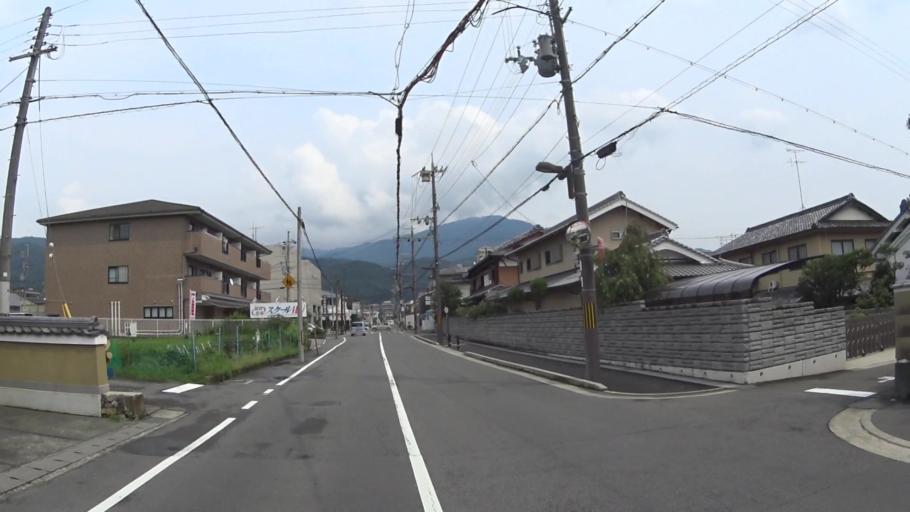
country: JP
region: Kyoto
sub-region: Kyoto-shi
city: Kamigyo-ku
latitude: 35.0737
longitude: 135.7861
